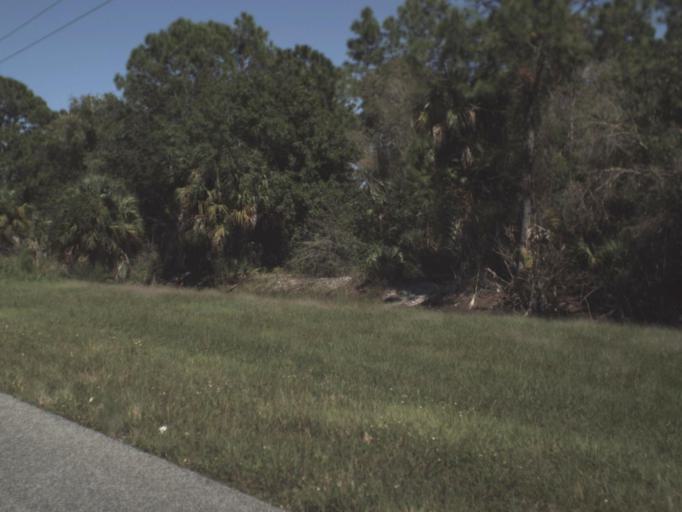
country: US
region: Florida
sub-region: Lee County
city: Palmona Park
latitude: 26.6925
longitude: -81.9009
